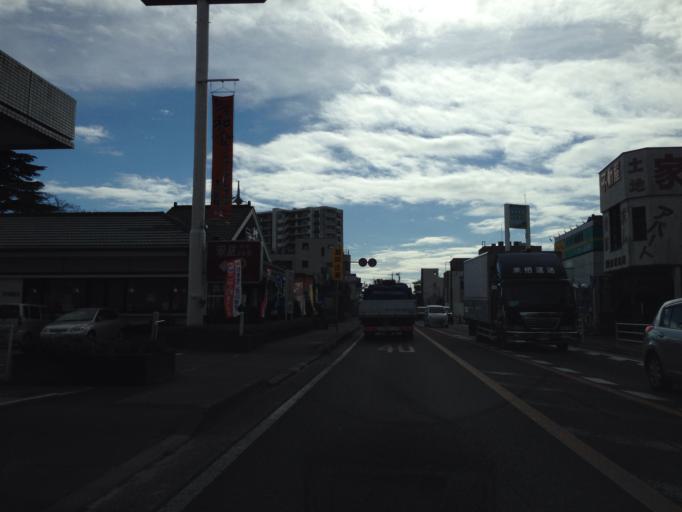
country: JP
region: Ibaraki
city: Ushiku
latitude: 35.9745
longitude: 140.1394
